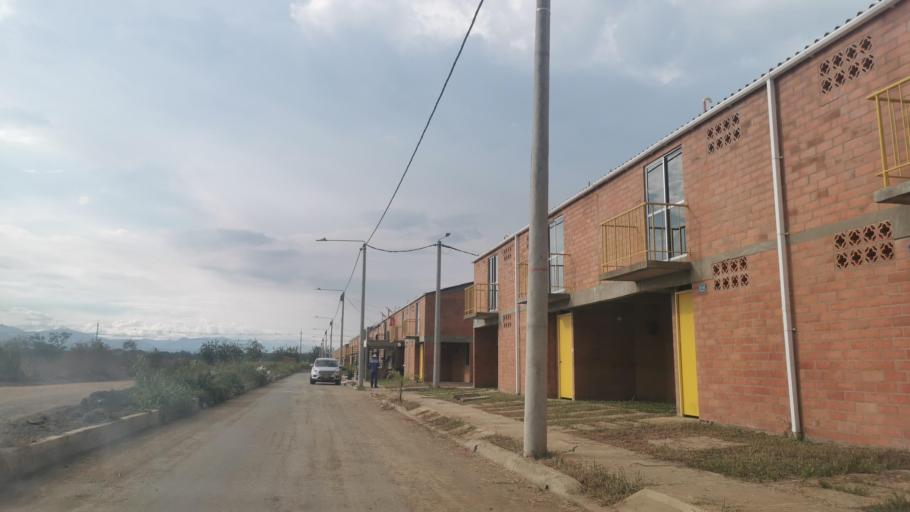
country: CO
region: Valle del Cauca
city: Jamundi
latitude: 3.2340
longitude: -76.5278
